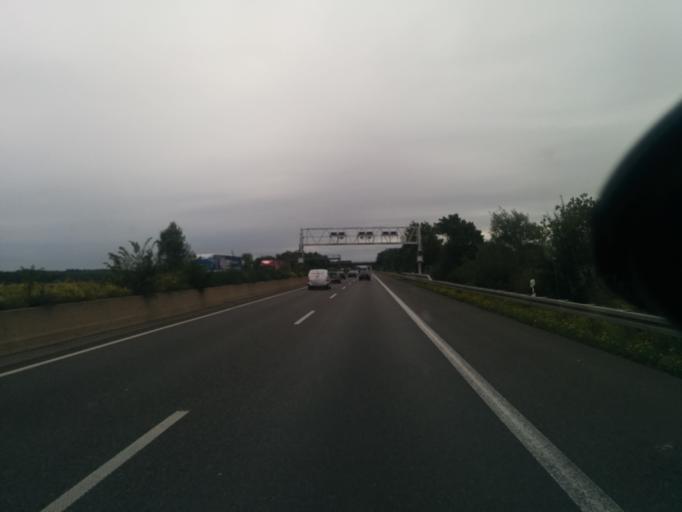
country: DE
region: North Rhine-Westphalia
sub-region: Regierungsbezirk Koln
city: Weilerswist
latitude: 50.7437
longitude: 6.8667
